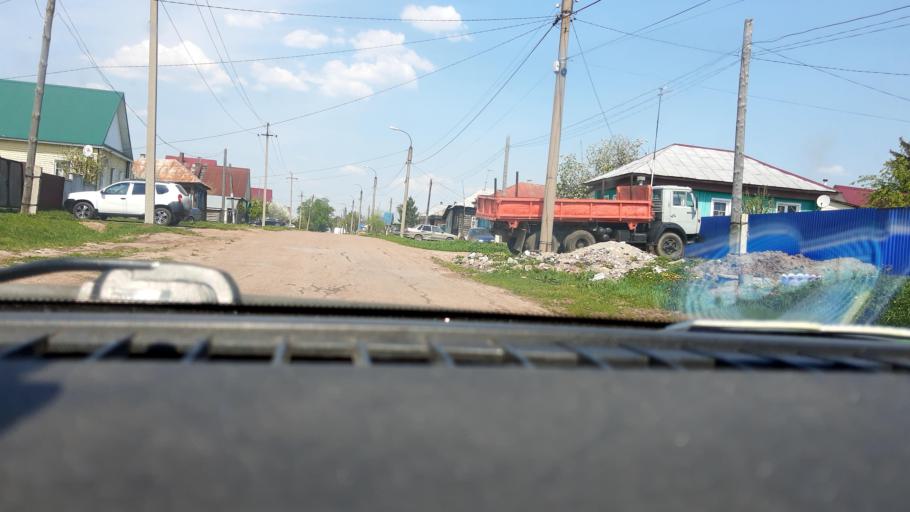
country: RU
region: Bashkortostan
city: Blagoveshchensk
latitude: 55.0233
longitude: 55.9837
